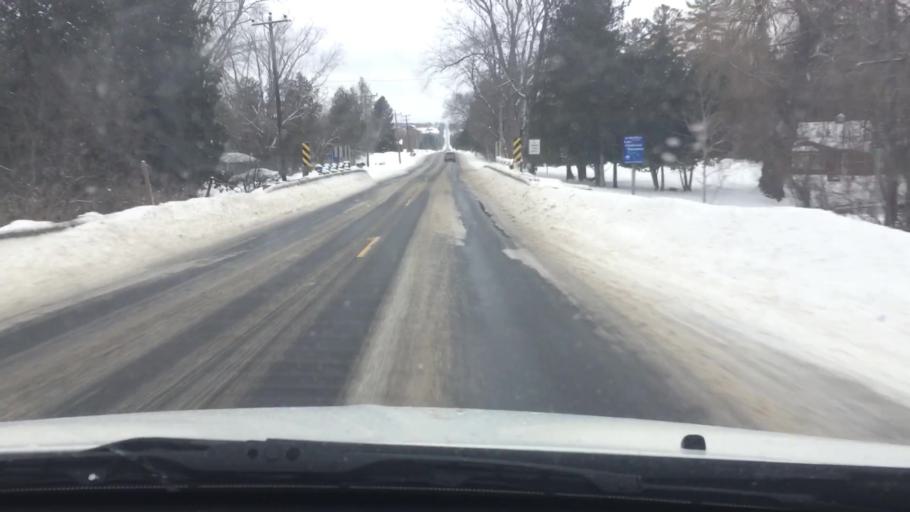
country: US
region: Michigan
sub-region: Charlevoix County
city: East Jordan
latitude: 45.1326
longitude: -85.1236
